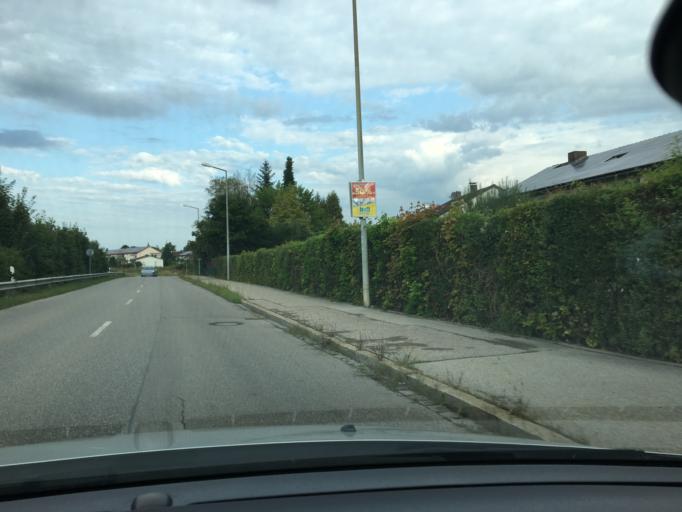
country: DE
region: Bavaria
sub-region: Upper Bavaria
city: Muehldorf
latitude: 48.2477
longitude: 12.5376
